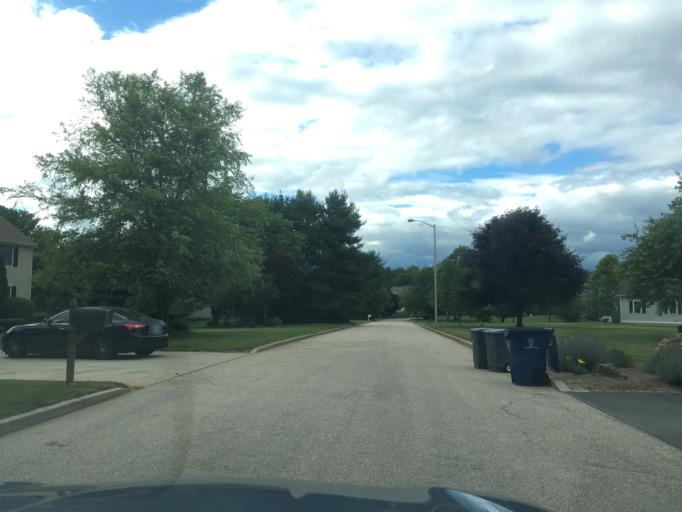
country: US
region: Rhode Island
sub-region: Washington County
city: Exeter
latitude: 41.6224
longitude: -71.5069
